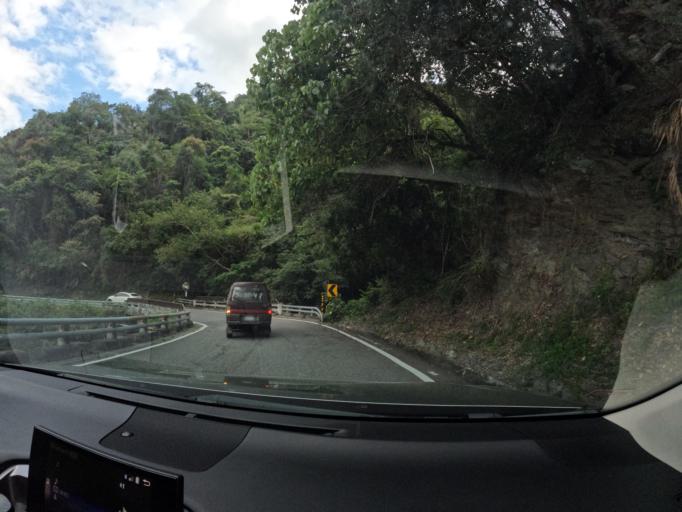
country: TW
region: Taiwan
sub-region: Taitung
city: Taitung
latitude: 23.1431
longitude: 121.0796
